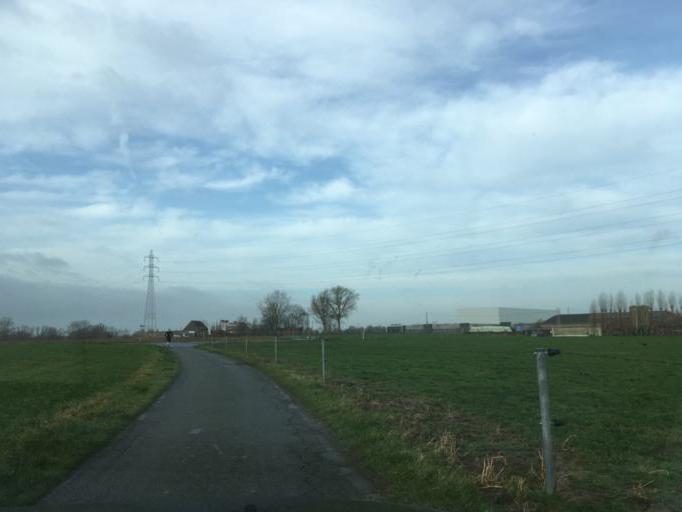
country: BE
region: Flanders
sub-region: Provincie West-Vlaanderen
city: Hooglede
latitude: 50.9637
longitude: 3.0903
